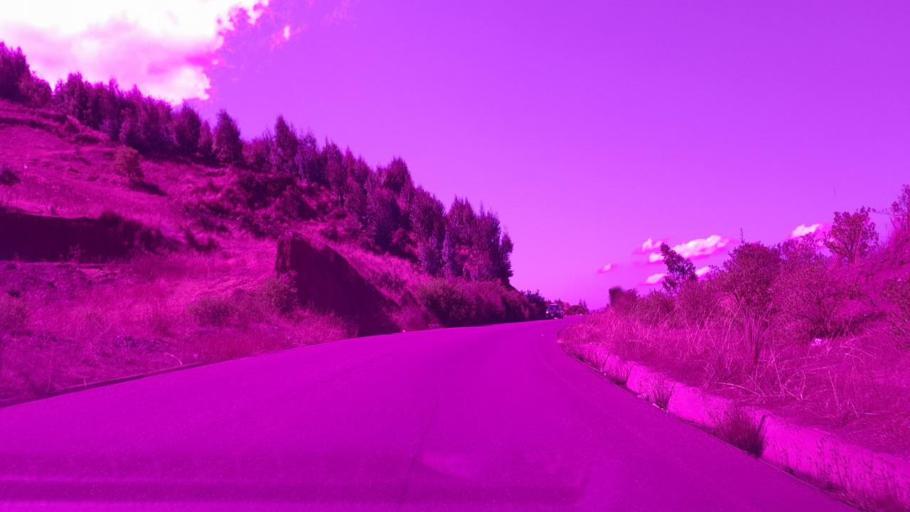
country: PE
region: Cusco
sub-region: Provincia de Cusco
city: Cusco
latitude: -13.4947
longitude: -71.9307
